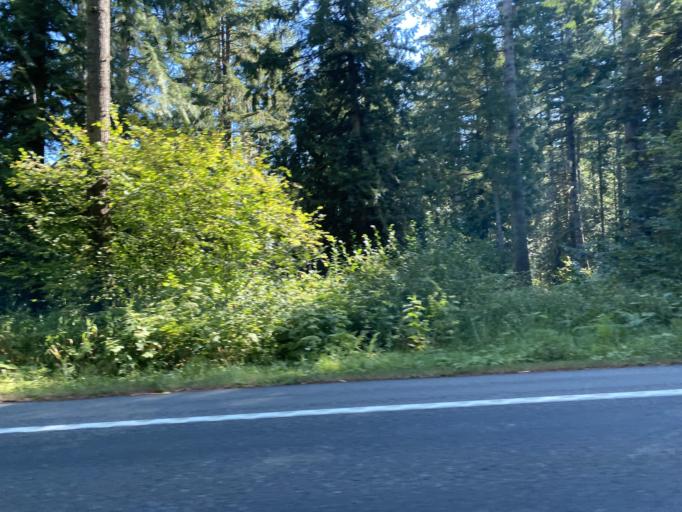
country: US
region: Washington
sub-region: Thurston County
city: Rainier
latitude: 46.9384
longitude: -122.7644
